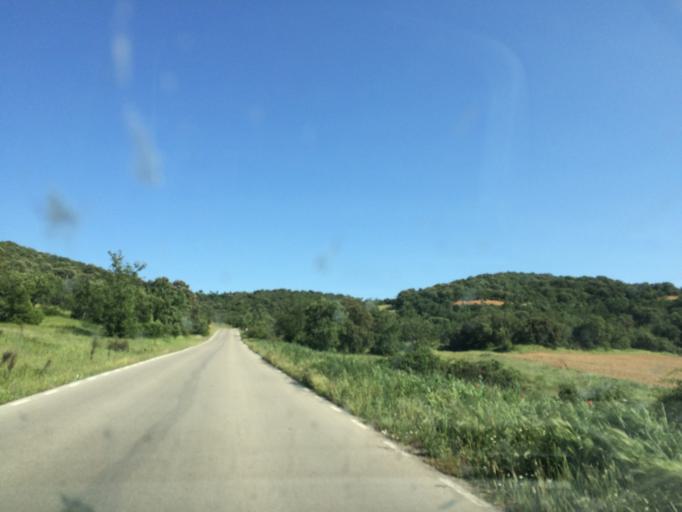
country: ES
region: Madrid
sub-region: Provincia de Madrid
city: Valdepielagos
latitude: 40.7607
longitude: -3.4147
